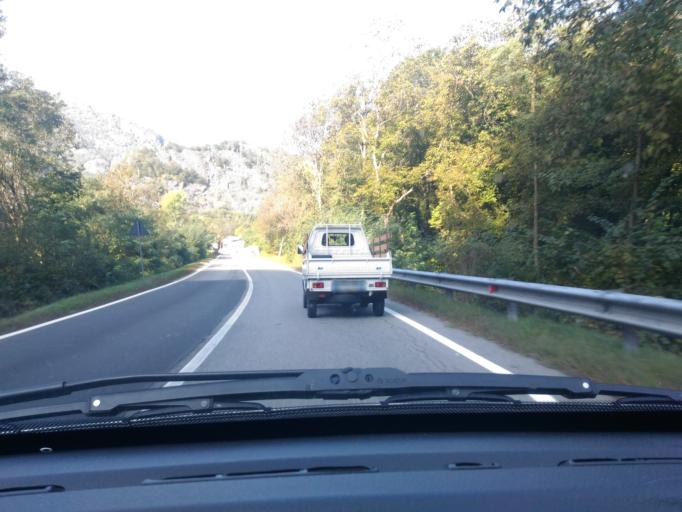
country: IT
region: Piedmont
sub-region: Provincia di Vercelli
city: Varallo
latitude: 45.8230
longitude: 8.2290
